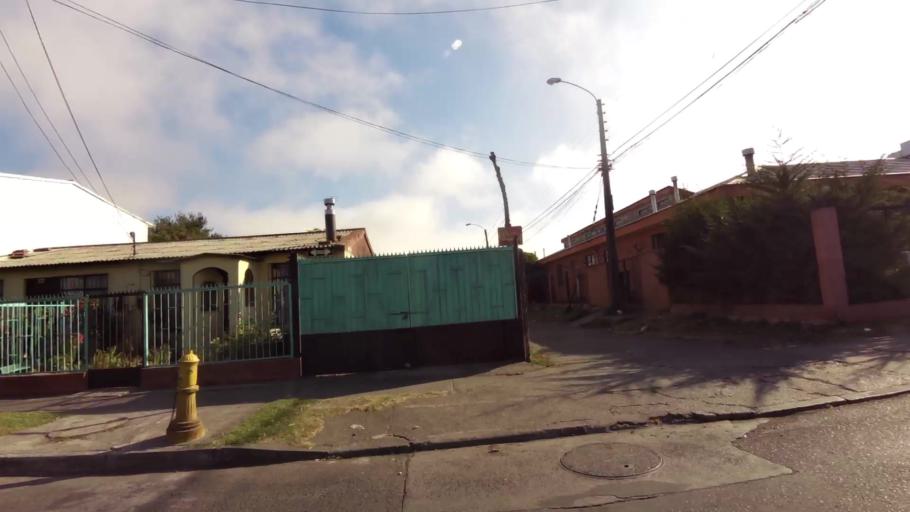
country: CL
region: Biobio
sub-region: Provincia de Concepcion
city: Concepcion
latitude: -36.7967
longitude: -73.1031
